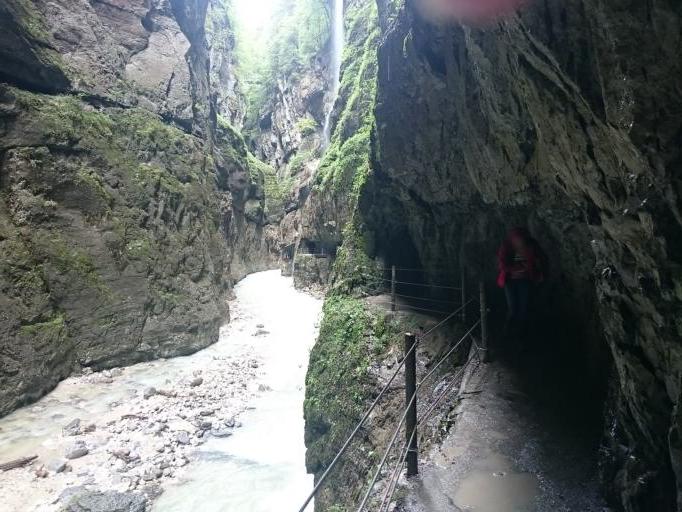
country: DE
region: Bavaria
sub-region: Upper Bavaria
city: Garmisch-Partenkirchen
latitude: 47.4640
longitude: 11.1231
